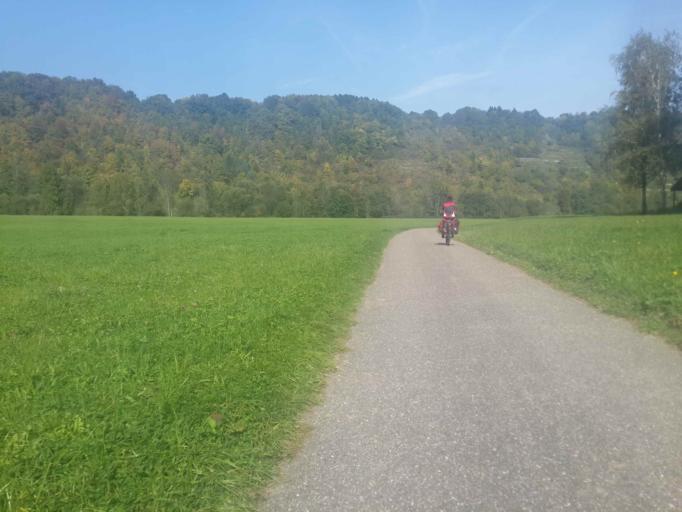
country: DE
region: Baden-Wuerttemberg
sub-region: Regierungsbezirk Stuttgart
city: Widdern
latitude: 49.3187
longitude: 9.3999
